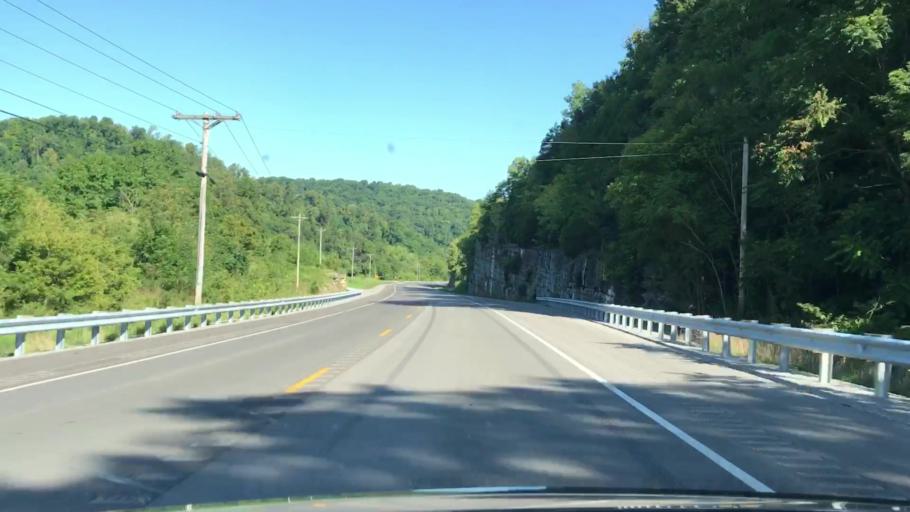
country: US
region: Kentucky
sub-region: Cumberland County
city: Burkesville
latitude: 36.7235
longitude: -85.3683
